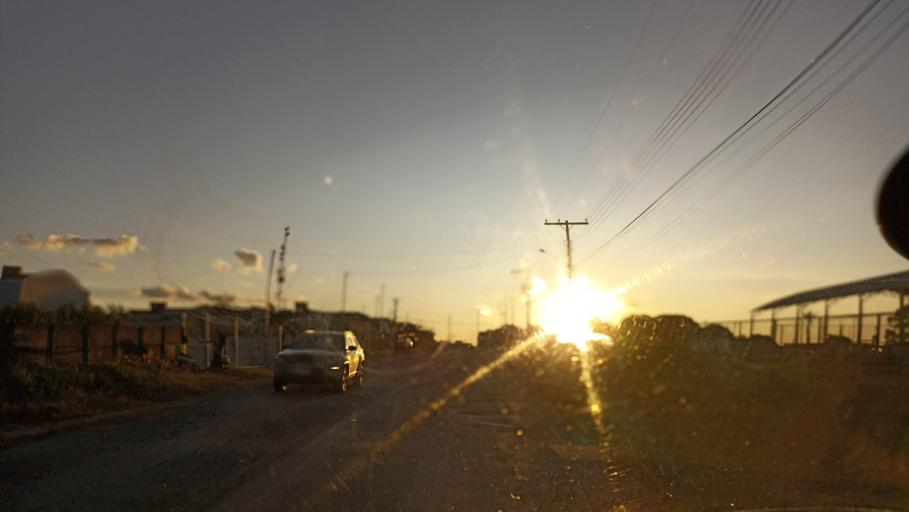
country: BR
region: Minas Gerais
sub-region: Sao Joao Del Rei
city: Sao Joao del Rei
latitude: -21.2435
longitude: -44.4059
